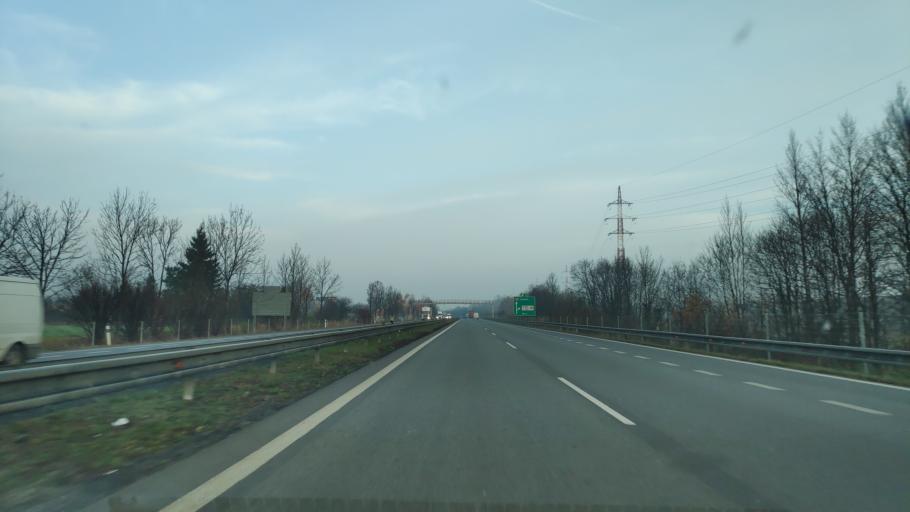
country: CZ
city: Paskov
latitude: 49.7443
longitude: 18.2799
